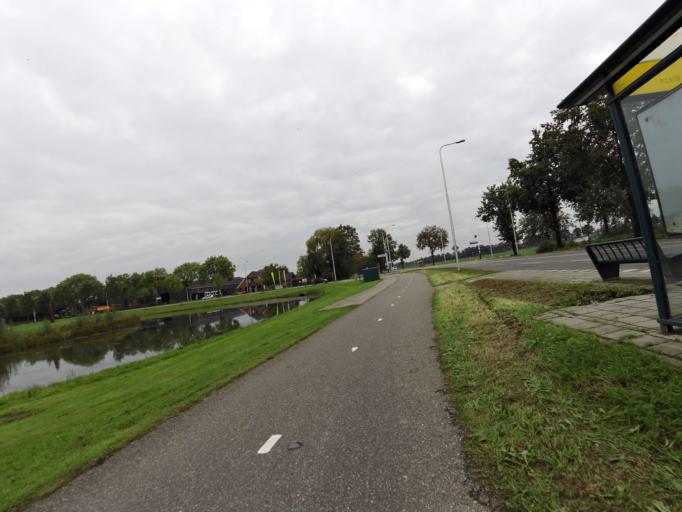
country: NL
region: Gelderland
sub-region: Oude IJsselstreek
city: Gendringen
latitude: 51.8985
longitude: 6.3570
